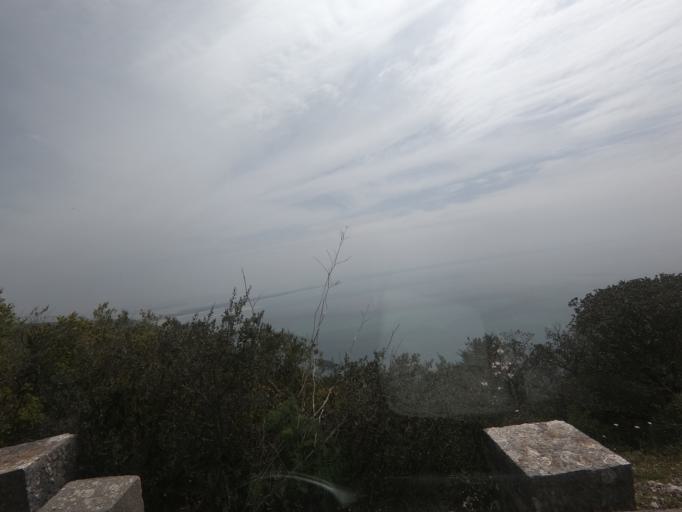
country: PT
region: Setubal
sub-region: Palmela
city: Quinta do Anjo
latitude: 38.4822
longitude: -8.9890
